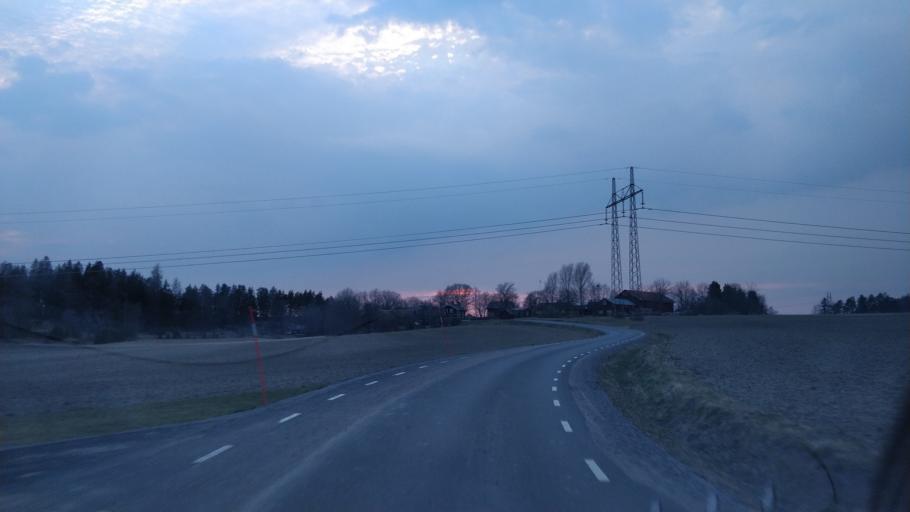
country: SE
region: Uppsala
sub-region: Enkopings Kommun
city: Orsundsbro
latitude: 59.7215
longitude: 17.2315
